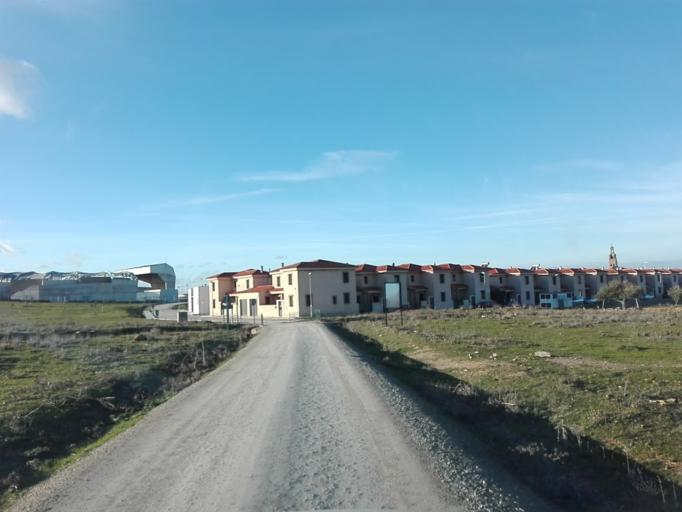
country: ES
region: Extremadura
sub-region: Provincia de Badajoz
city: Llerena
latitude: 38.2308
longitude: -6.0142
